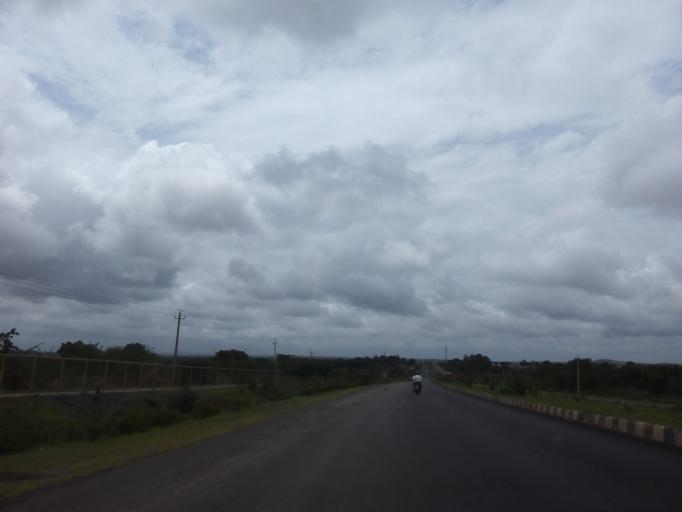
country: IN
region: Karnataka
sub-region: Haveri
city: Byadgi
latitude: 14.7013
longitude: 75.5226
